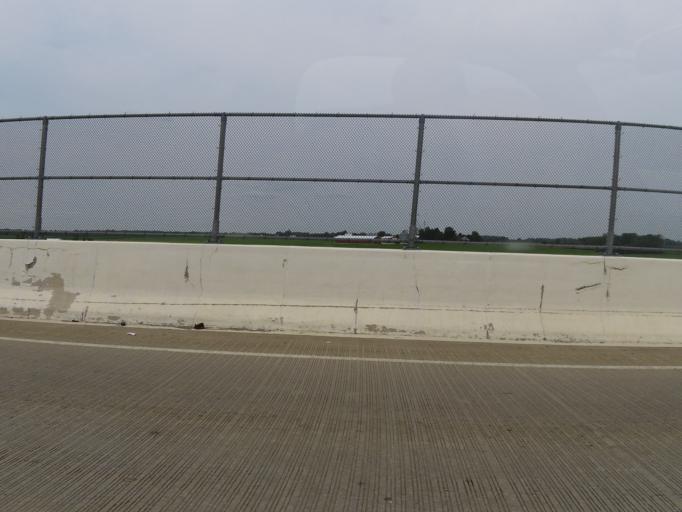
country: US
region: Ohio
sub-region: Clinton County
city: Wilmington
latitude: 39.4856
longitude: -83.9418
